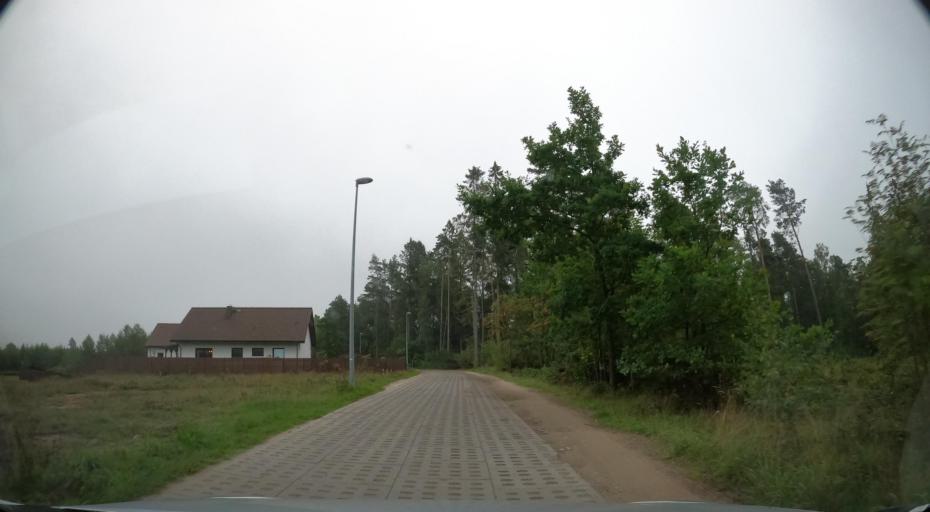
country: PL
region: Pomeranian Voivodeship
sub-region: Powiat kartuski
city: Chwaszczyno
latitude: 54.4170
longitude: 18.4339
